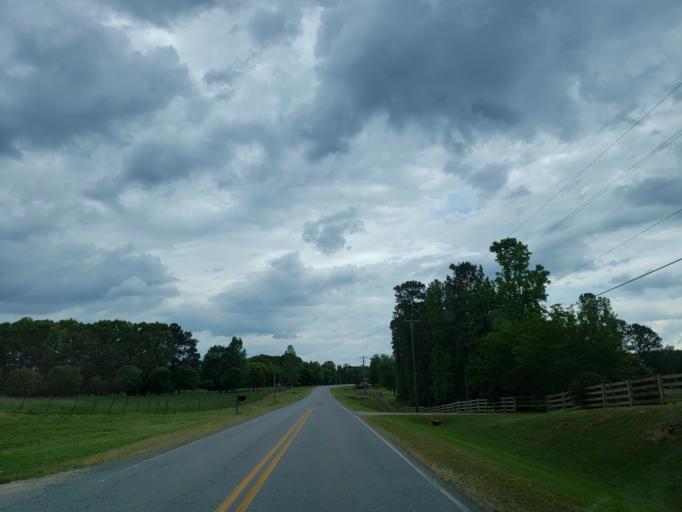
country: US
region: Georgia
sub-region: Polk County
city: Rockmart
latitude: 33.9228
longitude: -85.0625
